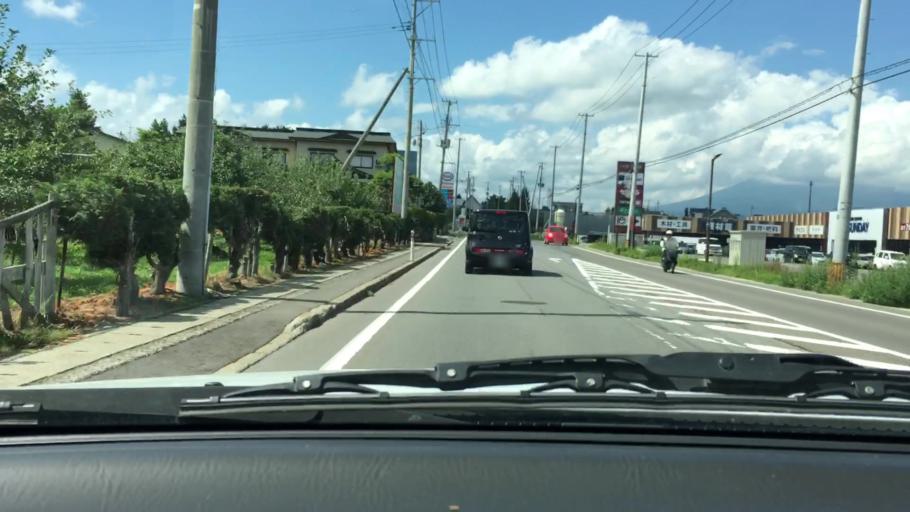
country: JP
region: Aomori
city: Hirosaki
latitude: 40.5869
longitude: 140.4605
